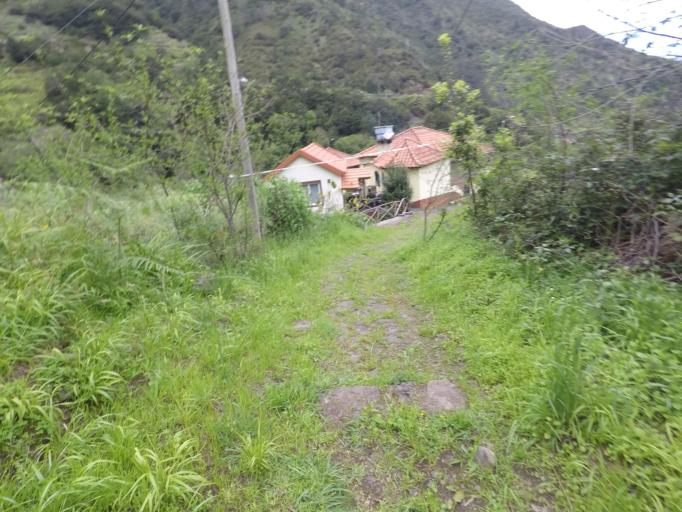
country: PT
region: Madeira
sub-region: Camara de Lobos
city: Curral das Freiras
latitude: 32.7802
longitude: -16.9798
